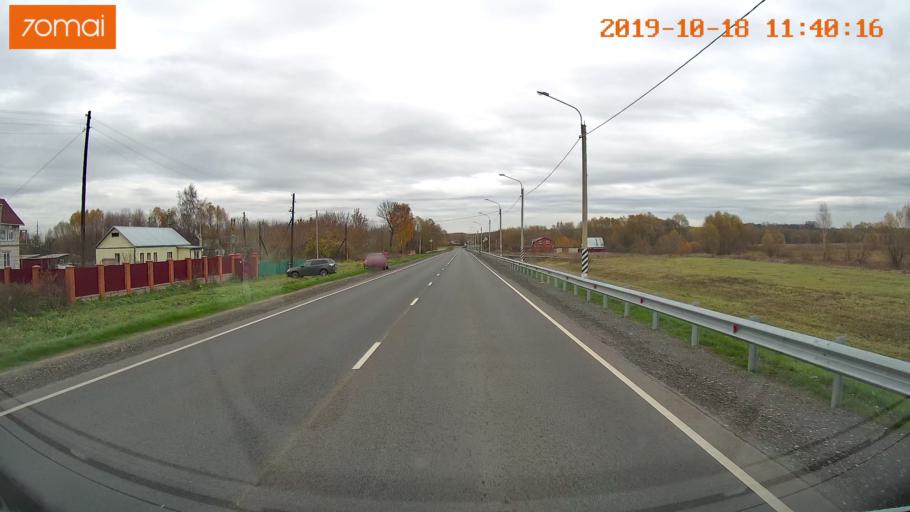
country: RU
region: Rjazan
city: Oktyabr'skiy
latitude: 54.1786
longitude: 38.8882
